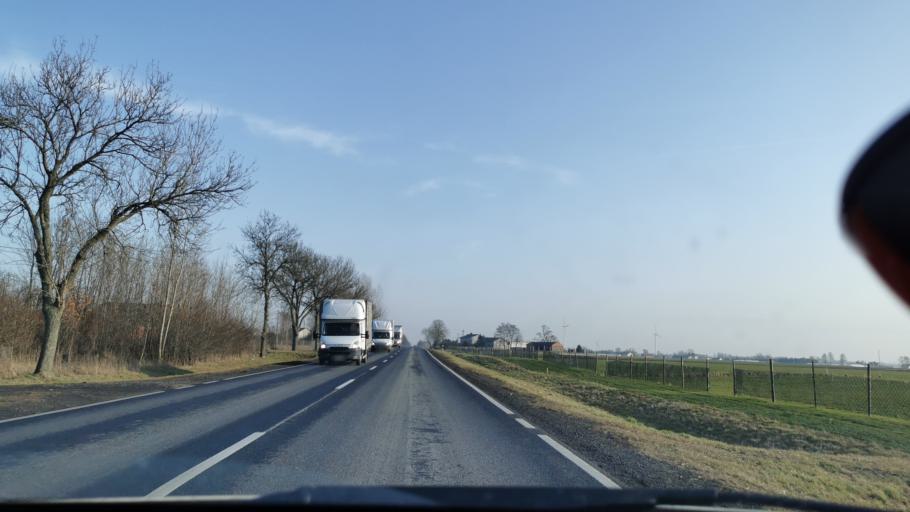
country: PL
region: Lodz Voivodeship
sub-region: Powiat sieradzki
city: Blaszki
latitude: 51.6739
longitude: 18.3629
